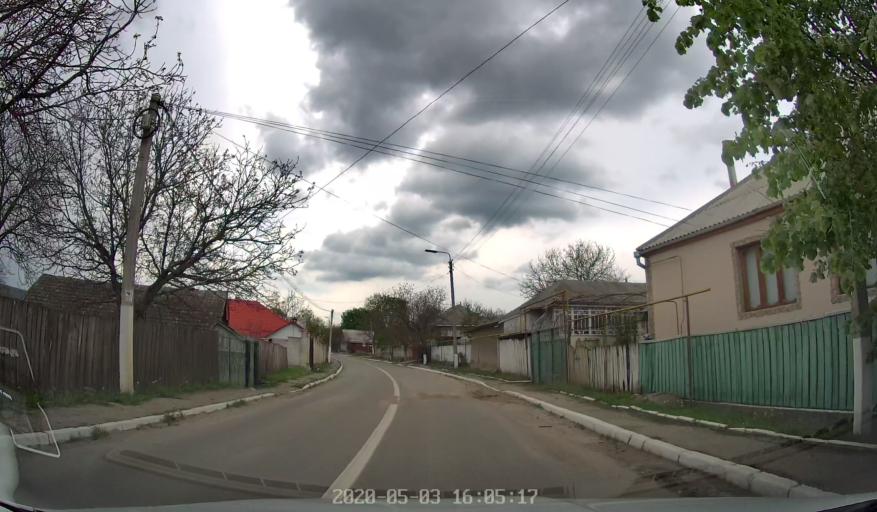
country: MD
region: Calarasi
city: Calarasi
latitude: 47.1897
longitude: 28.3585
